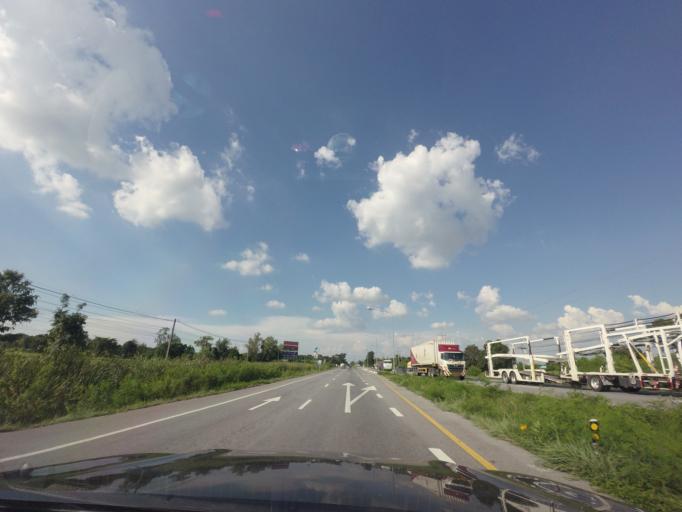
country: TH
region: Khon Kaen
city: Phon
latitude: 15.7205
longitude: 102.5915
